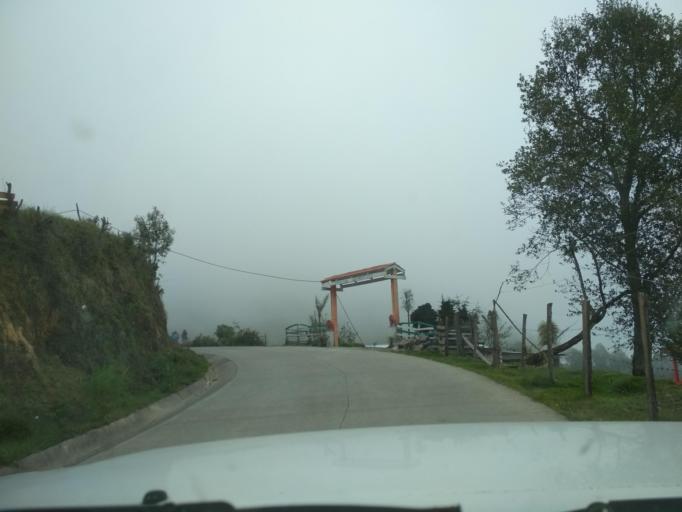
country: MX
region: Veracruz
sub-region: La Perla
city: Chilapa
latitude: 18.9819
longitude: -97.1913
